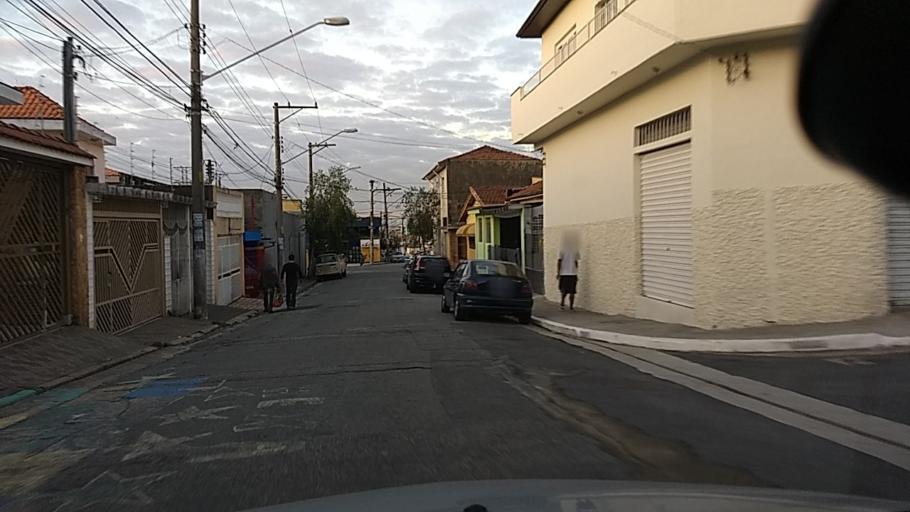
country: BR
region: Sao Paulo
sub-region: Guarulhos
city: Guarulhos
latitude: -23.4962
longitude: -46.5869
